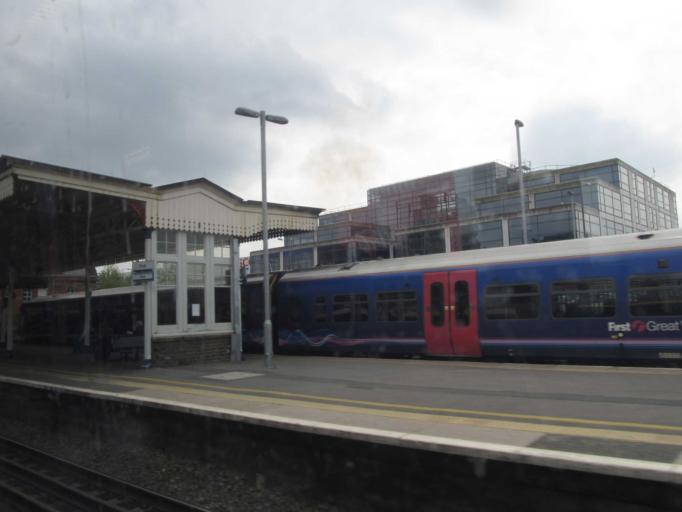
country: GB
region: England
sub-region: Slough
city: Slough
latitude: 51.5121
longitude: -0.5923
